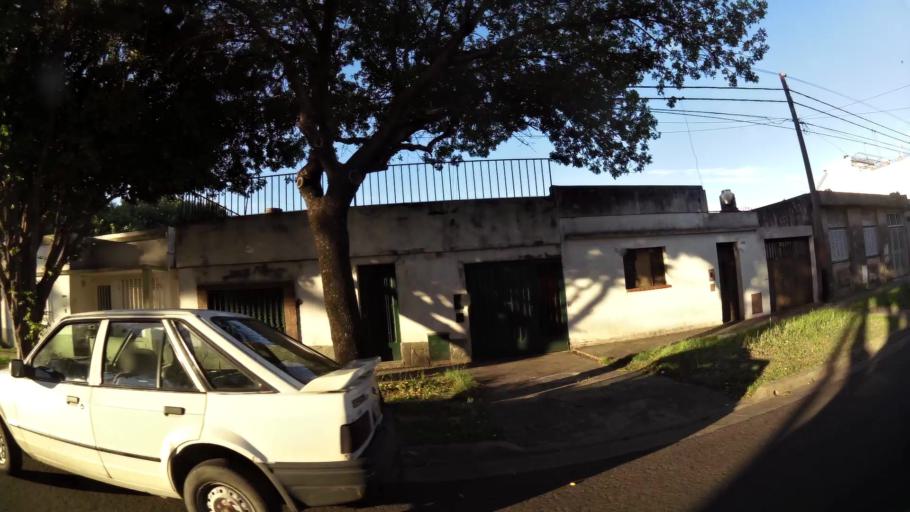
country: AR
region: Santa Fe
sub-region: Departamento de Rosario
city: Rosario
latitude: -32.9736
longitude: -60.6705
